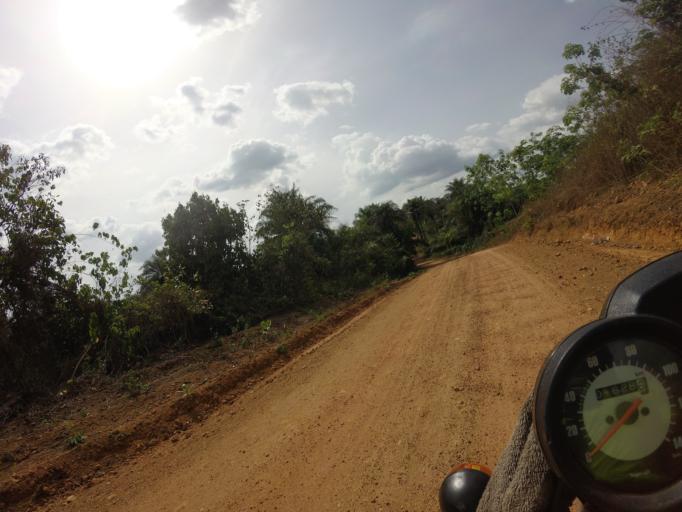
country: SL
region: Southern Province
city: Zimmi
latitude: 7.2308
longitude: -11.1960
